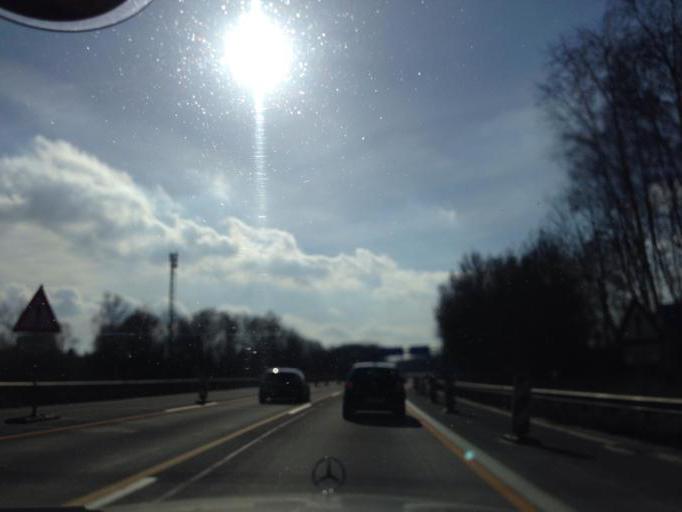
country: DE
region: Lower Saxony
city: Harmstorf
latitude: 53.3861
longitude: 10.0202
